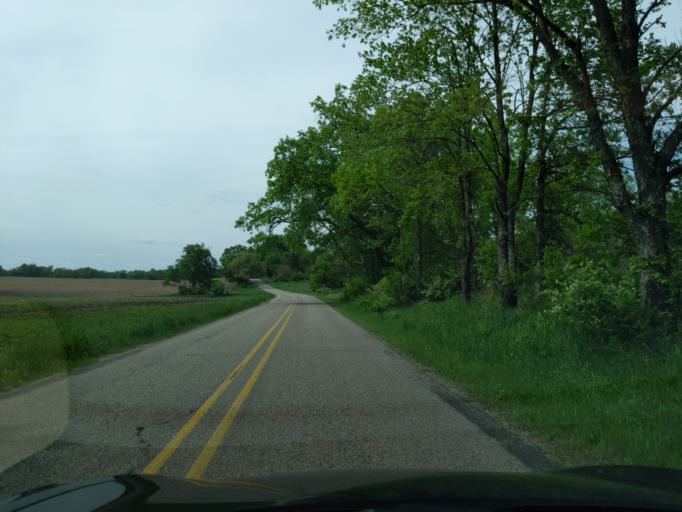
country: US
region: Michigan
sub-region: Ingham County
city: Leslie
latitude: 42.4275
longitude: -84.3351
